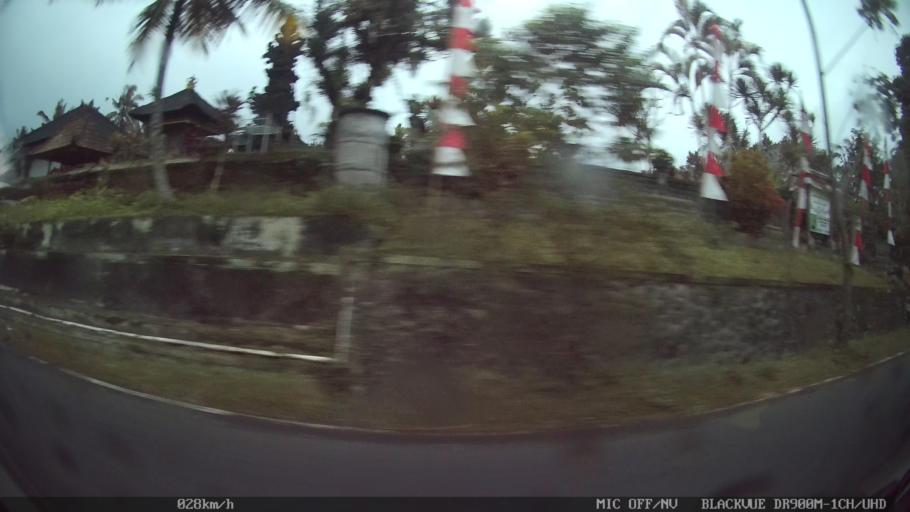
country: ID
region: Bali
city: Banjar Ponggang
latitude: -8.3970
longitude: 115.2504
